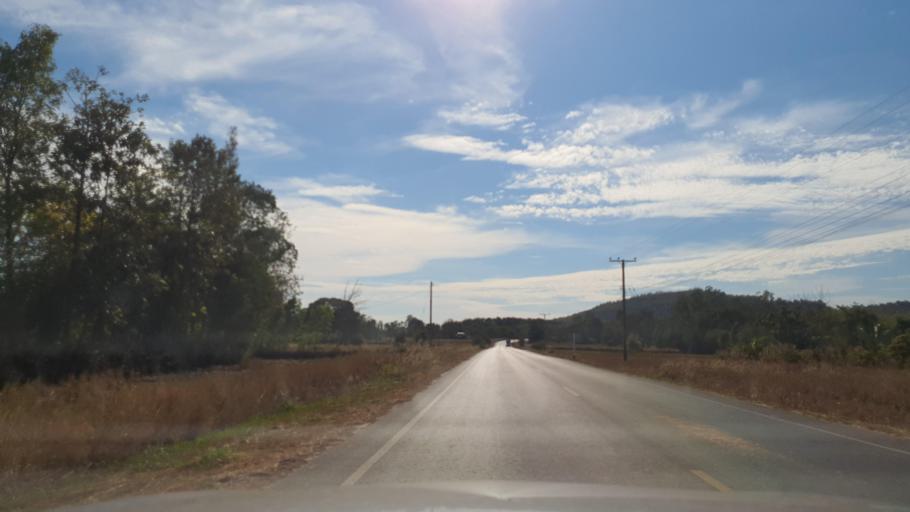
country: TH
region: Kalasin
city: Kuchinarai
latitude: 16.5870
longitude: 104.1281
